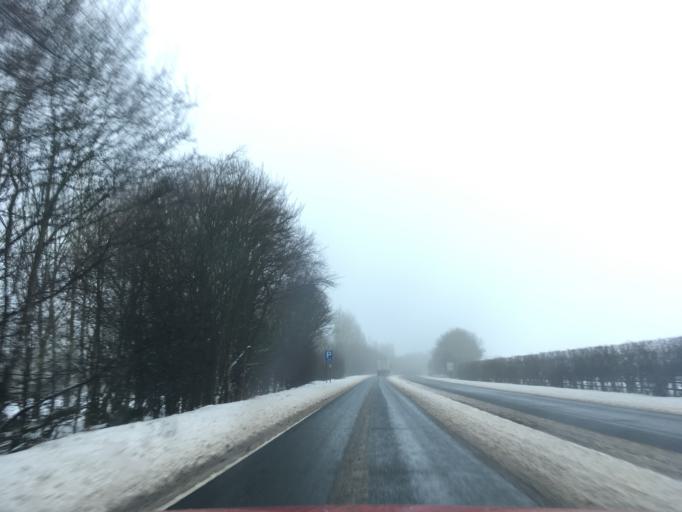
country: GB
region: England
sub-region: Warwickshire
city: Stratford-upon-Avon
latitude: 52.2359
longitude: -1.6717
